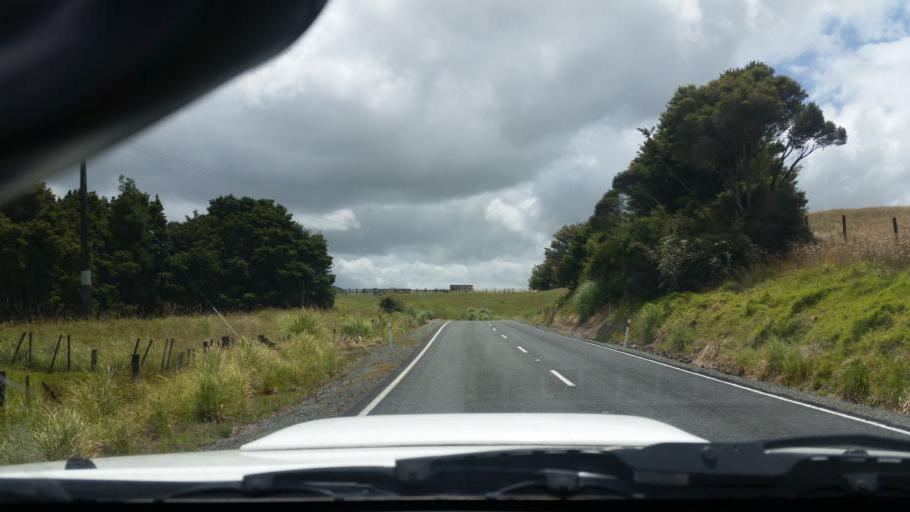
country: NZ
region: Auckland
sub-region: Auckland
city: Wellsford
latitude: -36.1277
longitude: 174.3281
